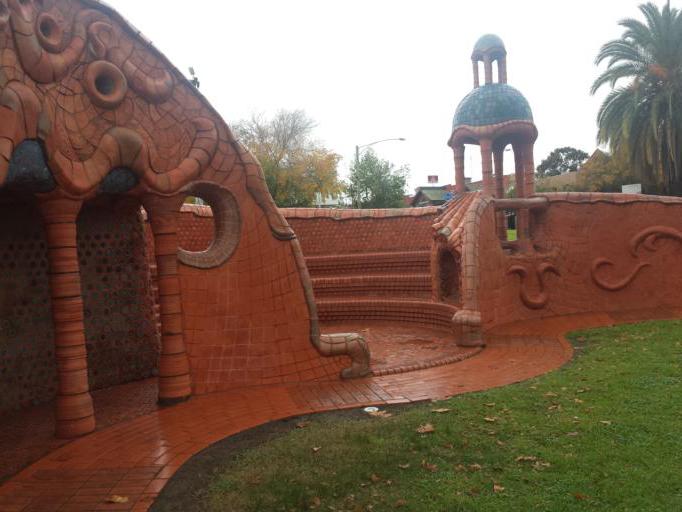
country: AU
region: Victoria
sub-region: Benalla
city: Benalla
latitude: -36.5519
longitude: 145.9814
